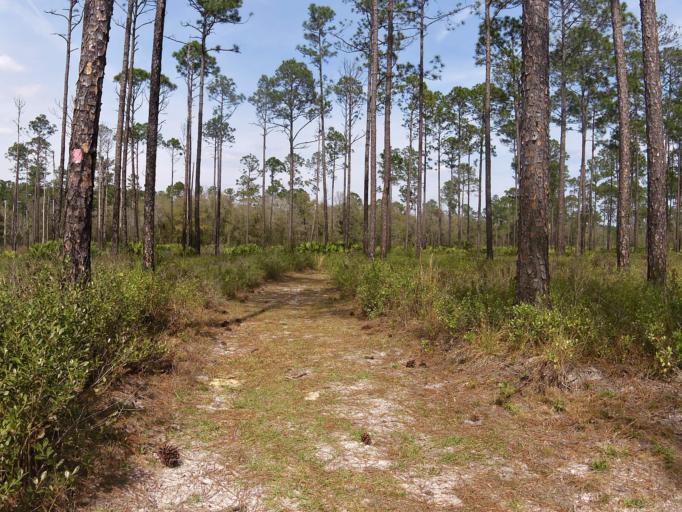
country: US
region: Florida
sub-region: Clay County
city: Middleburg
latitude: 30.1228
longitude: -81.8849
